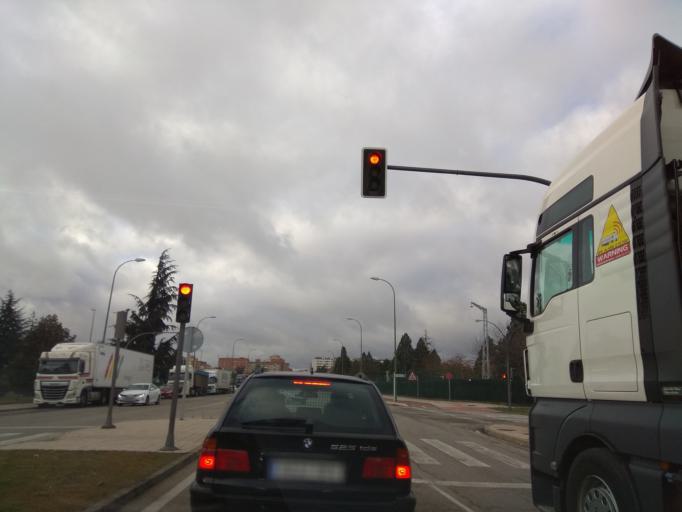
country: ES
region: Castille and Leon
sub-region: Provincia de Burgos
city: Burgos
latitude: 42.3571
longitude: -3.6562
